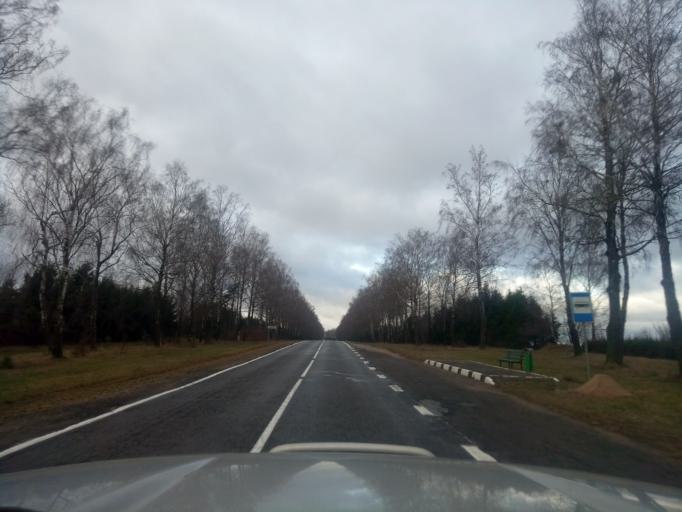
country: BY
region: Minsk
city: Slutsk
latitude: 53.2209
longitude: 27.5083
